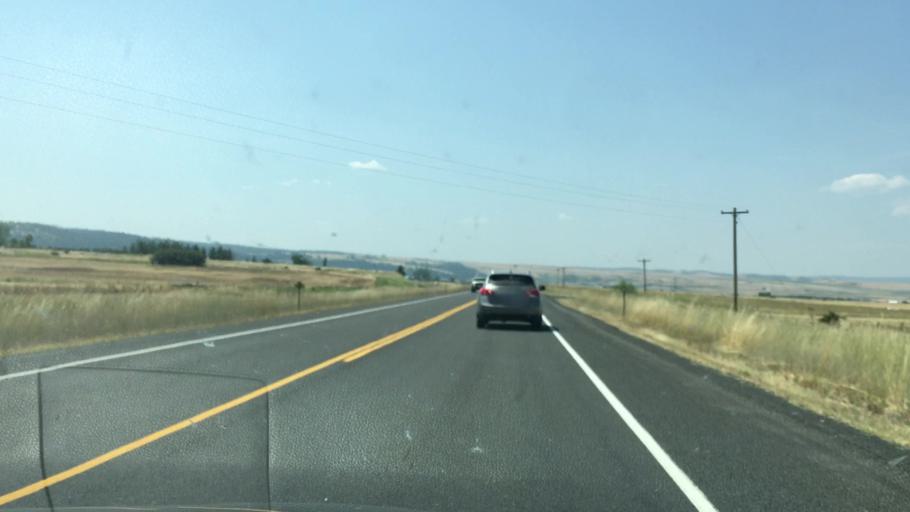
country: US
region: Idaho
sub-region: Idaho County
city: Grangeville
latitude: 45.9109
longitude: -116.1654
